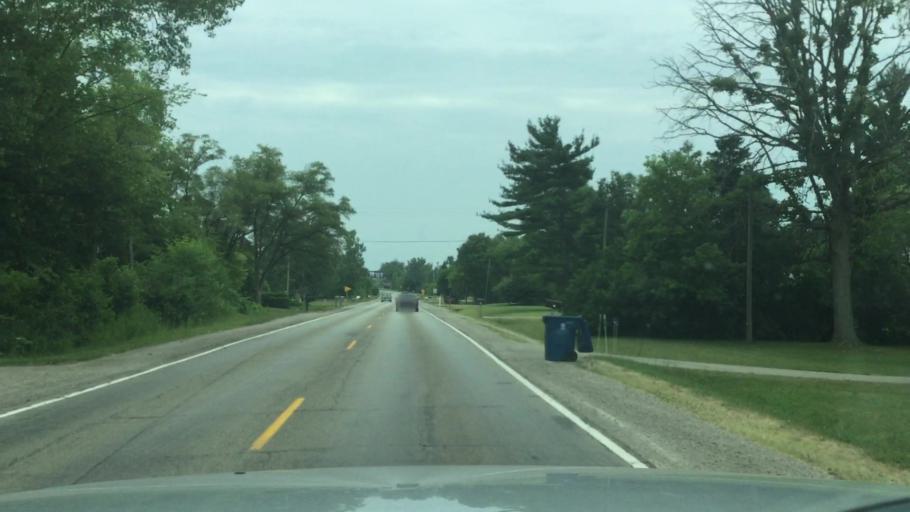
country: US
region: Michigan
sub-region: Genesee County
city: Flint
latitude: 42.9493
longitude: -83.7123
